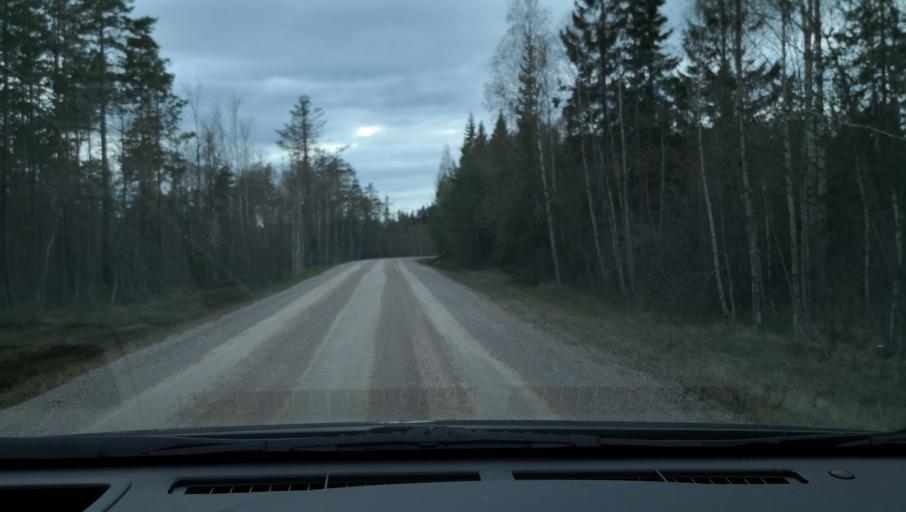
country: SE
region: Vaestmanland
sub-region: Norbergs Kommun
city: Norberg
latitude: 60.0913
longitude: 15.8343
